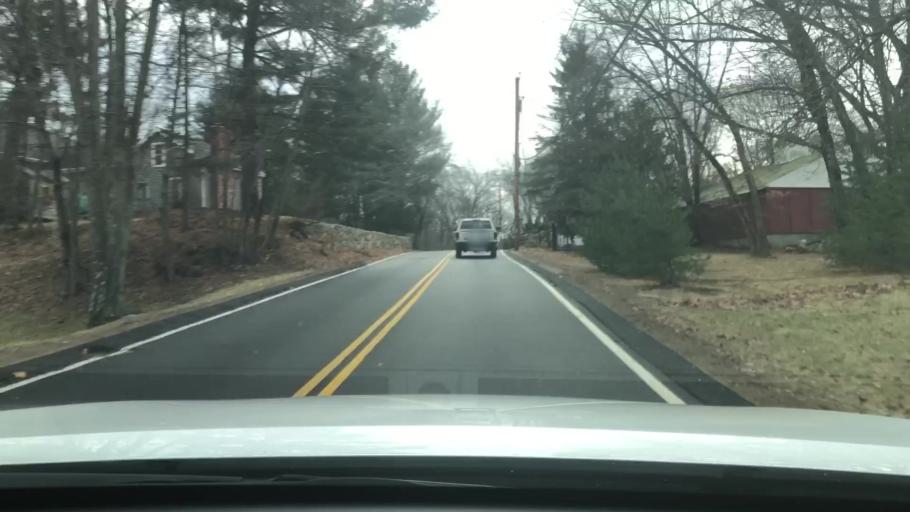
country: US
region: Massachusetts
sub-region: Worcester County
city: Blackstone
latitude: 42.0363
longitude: -71.5197
